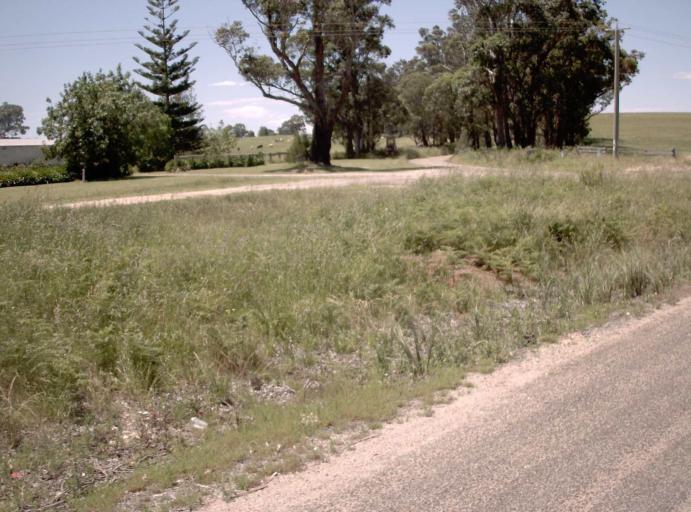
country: AU
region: Victoria
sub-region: East Gippsland
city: Lakes Entrance
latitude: -37.7030
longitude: 148.5176
